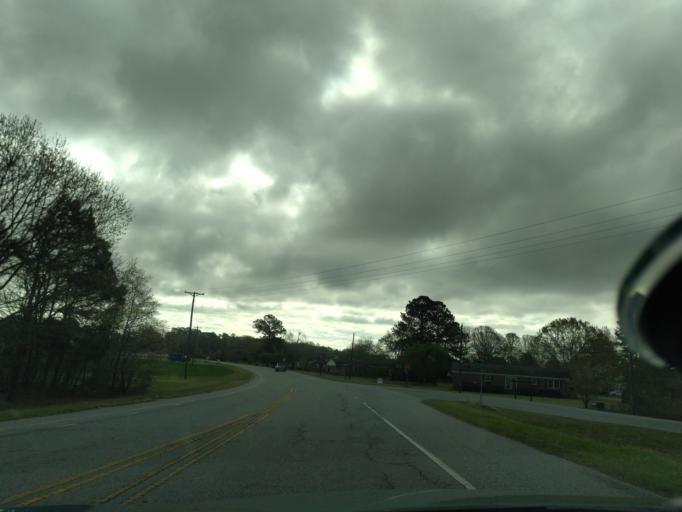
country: US
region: North Carolina
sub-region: Chowan County
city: Edenton
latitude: 36.0581
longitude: -76.6662
